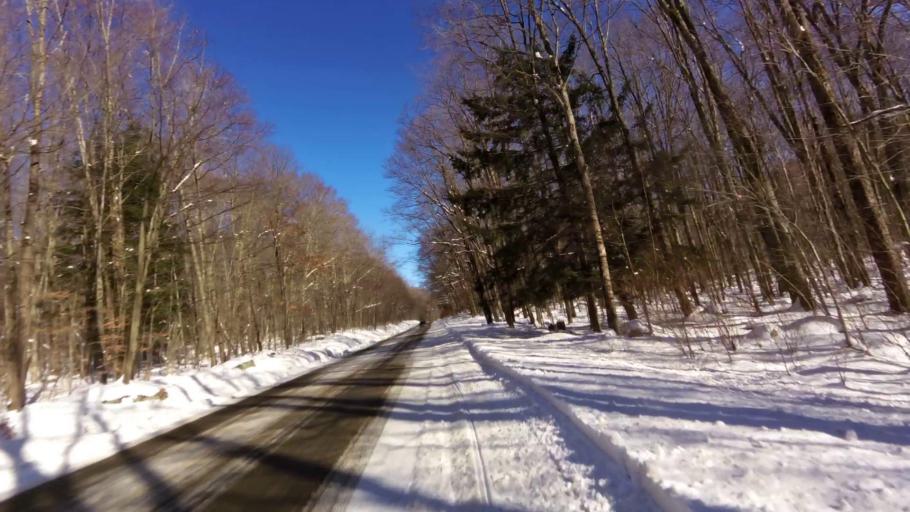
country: US
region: New York
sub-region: Cattaraugus County
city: Salamanca
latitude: 42.1173
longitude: -78.7345
